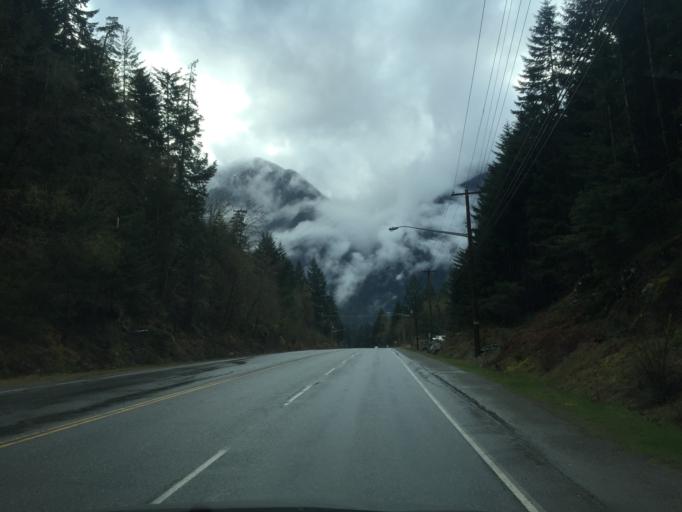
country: CA
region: British Columbia
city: Hope
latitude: 49.3656
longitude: -121.4507
